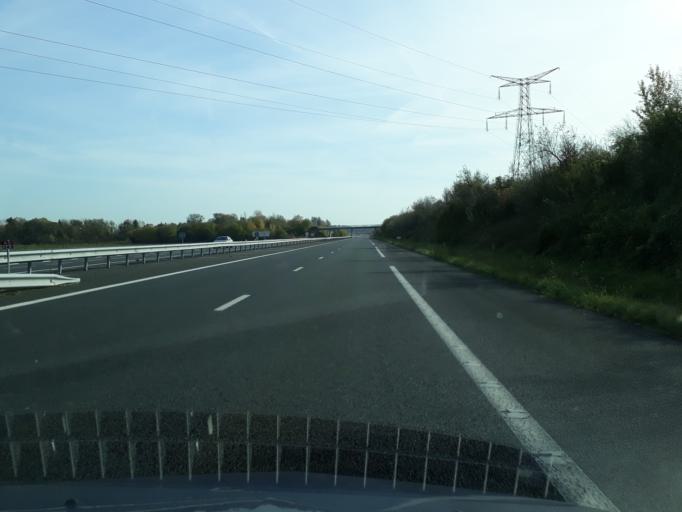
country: FR
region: Champagne-Ardenne
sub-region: Departement de l'Aube
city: Saint-Pouange
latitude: 48.2309
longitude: 4.0561
